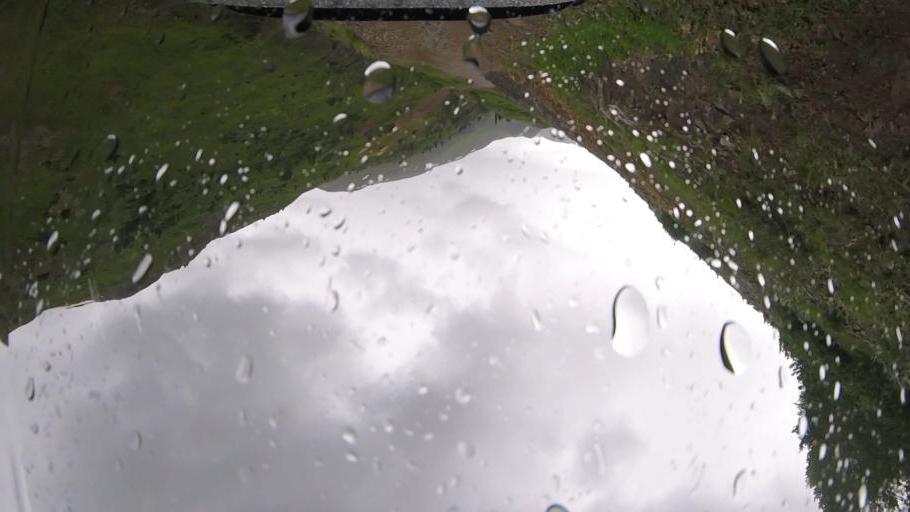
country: US
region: Colorado
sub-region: Ouray County
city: Ouray
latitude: 37.9422
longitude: -107.5736
